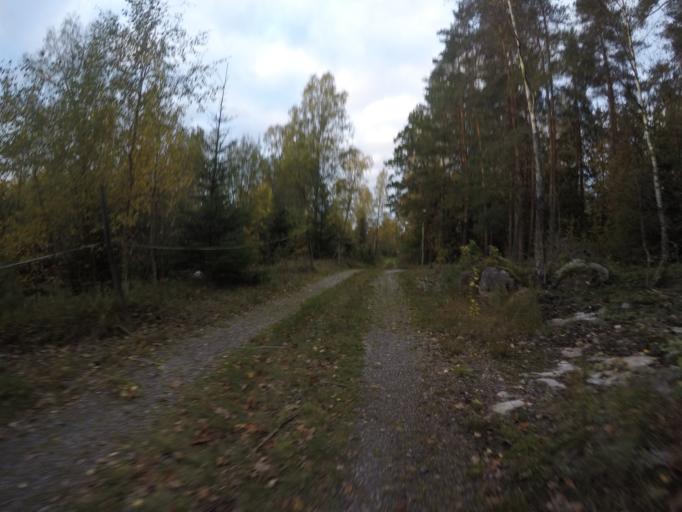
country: SE
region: Vaestmanland
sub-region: Arboga Kommun
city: Tyringe
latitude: 59.3211
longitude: 15.9742
